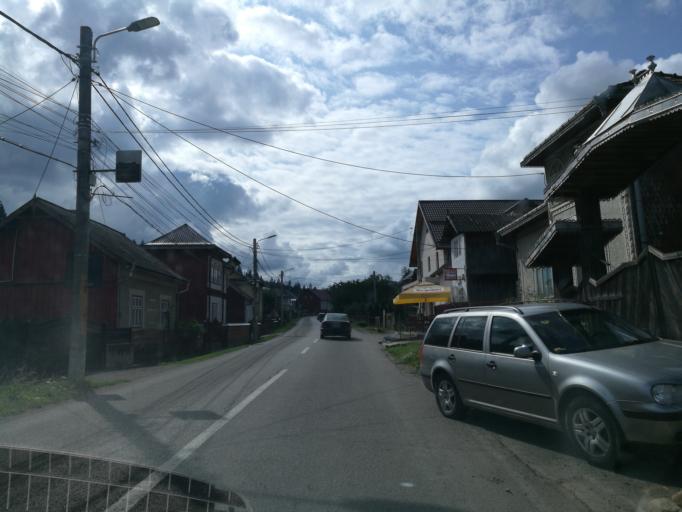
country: RO
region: Suceava
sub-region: Oras Gura Humorului
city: Gura Humorului
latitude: 47.5273
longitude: 25.8639
